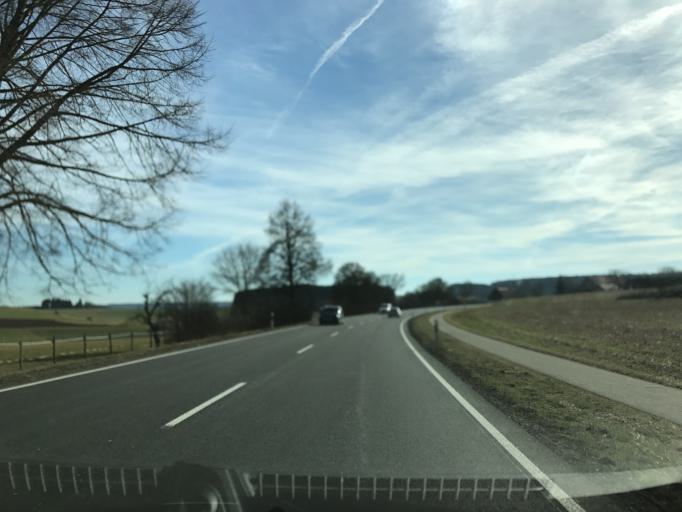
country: DE
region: Baden-Wuerttemberg
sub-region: Tuebingen Region
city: Eberhardzell
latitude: 47.9808
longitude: 9.7760
